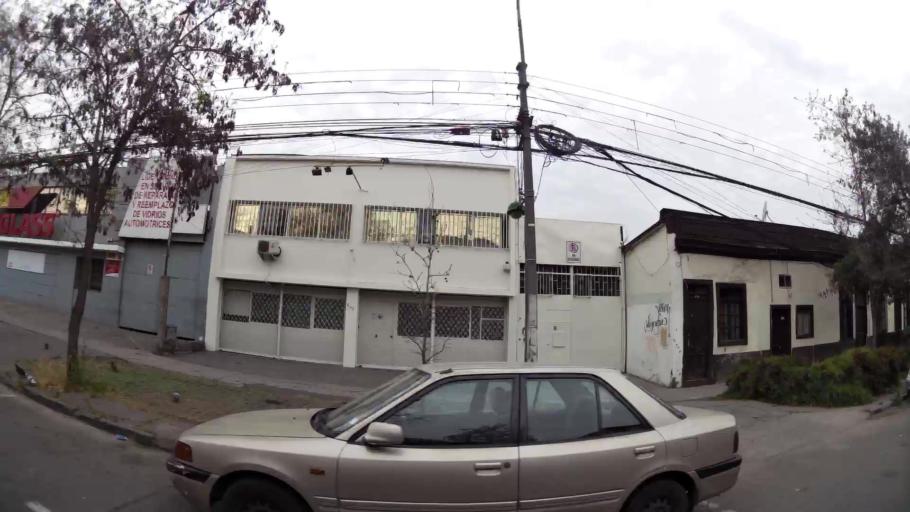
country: CL
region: Santiago Metropolitan
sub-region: Provincia de Santiago
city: Santiago
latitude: -33.4478
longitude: -70.6301
